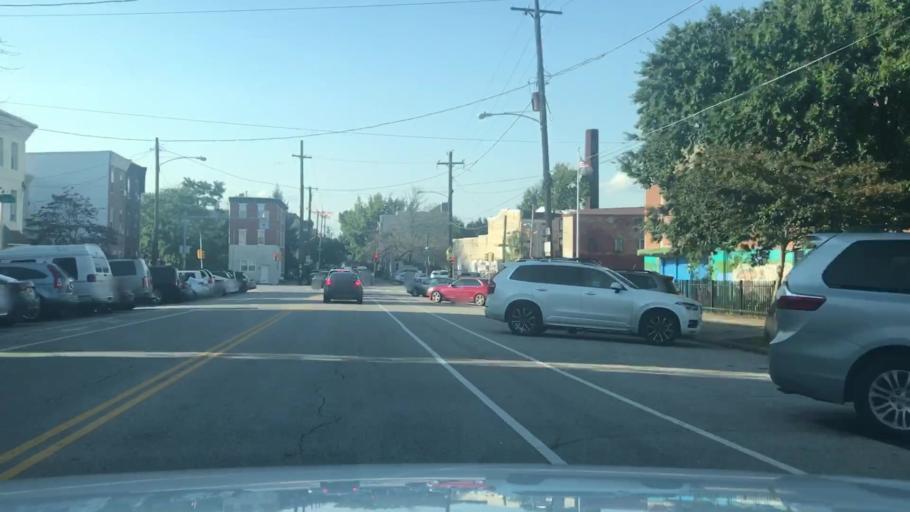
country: US
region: Pennsylvania
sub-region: Philadelphia County
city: Philadelphia
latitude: 39.9807
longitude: -75.1269
